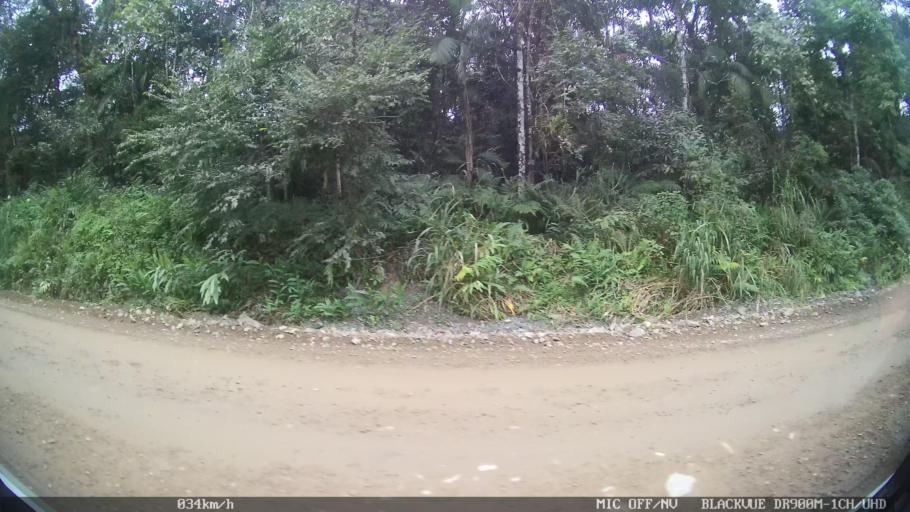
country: BR
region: Santa Catarina
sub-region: Joinville
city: Joinville
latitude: -26.2407
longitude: -48.9260
